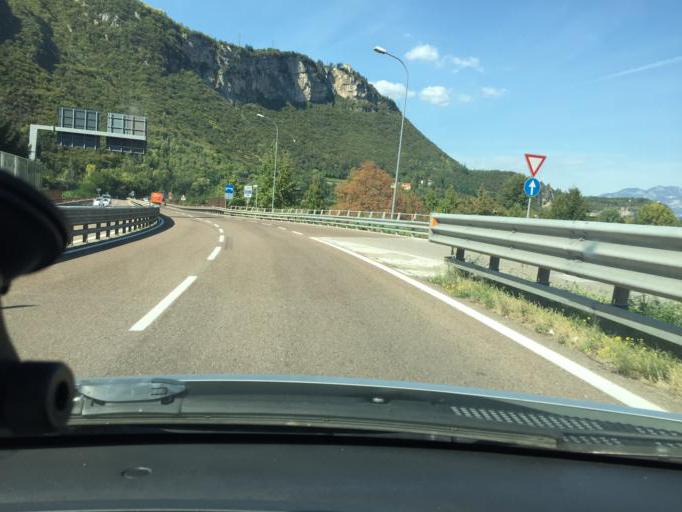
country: IT
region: Trentino-Alto Adige
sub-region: Provincia di Trento
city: Ravina
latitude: 46.0521
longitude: 11.1127
